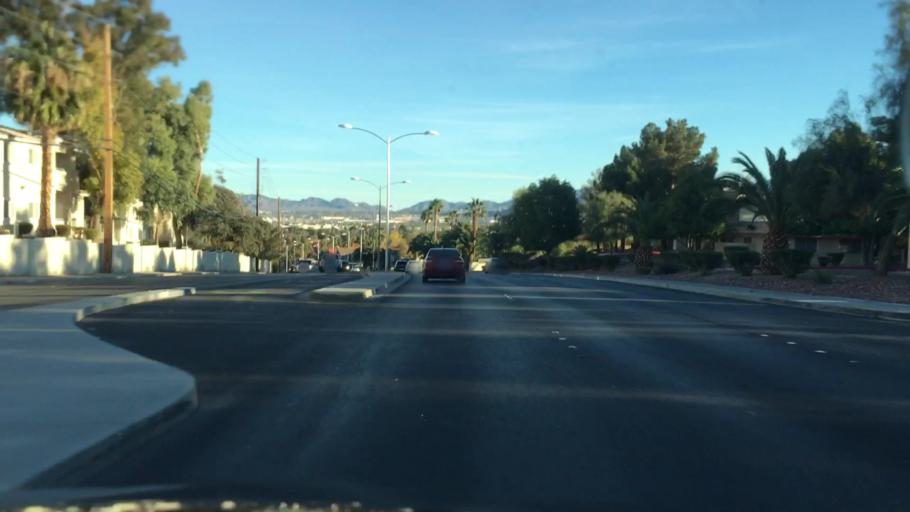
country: US
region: Nevada
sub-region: Clark County
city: Whitney
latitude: 36.0657
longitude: -115.0657
